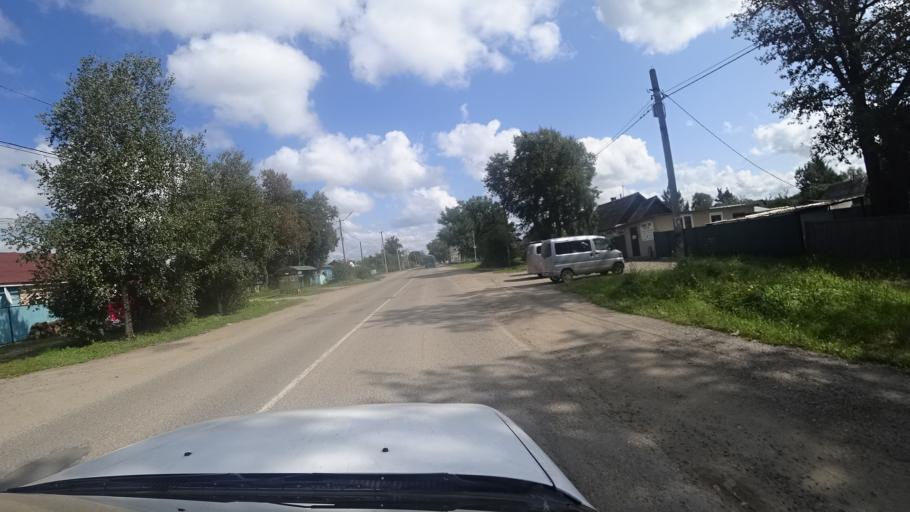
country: RU
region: Primorskiy
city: Dal'nerechensk
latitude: 45.9315
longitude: 133.7587
